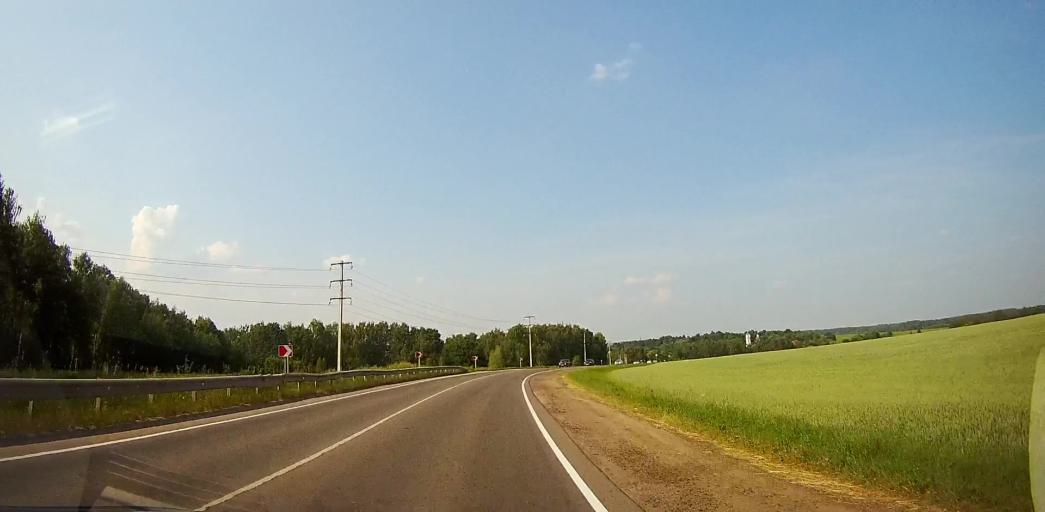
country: RU
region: Moskovskaya
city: Barybino
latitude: 55.2883
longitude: 37.9123
